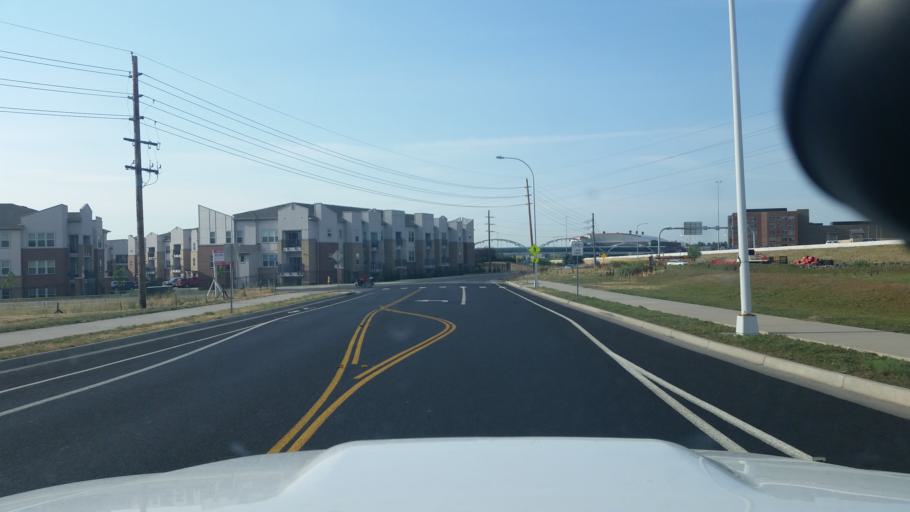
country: US
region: Colorado
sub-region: Broomfield County
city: Broomfield
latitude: 39.9103
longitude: -105.0860
